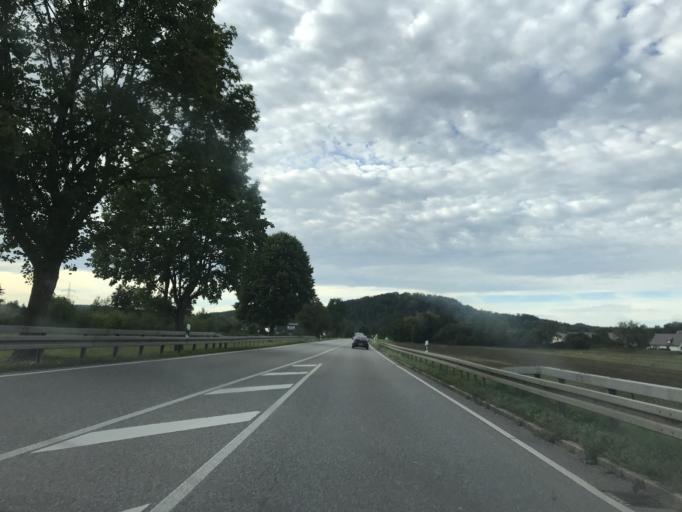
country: CH
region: Aargau
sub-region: Bezirk Rheinfelden
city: Mumpf
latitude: 47.5759
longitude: 7.9139
